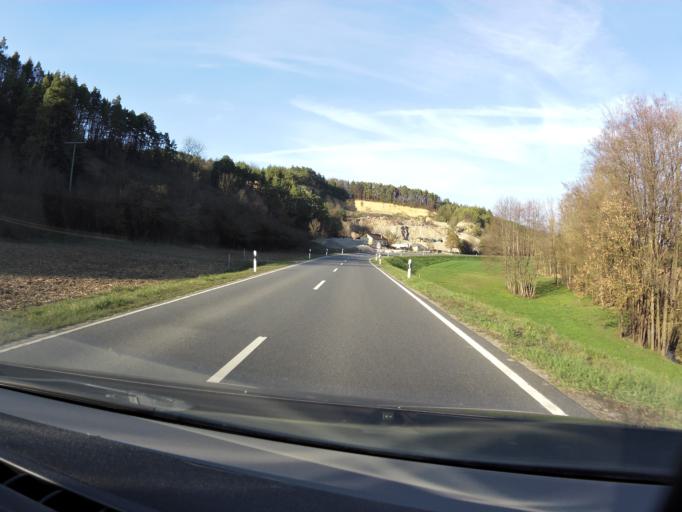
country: DE
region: Baden-Wuerttemberg
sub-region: Regierungsbezirk Stuttgart
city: Bad Mergentheim
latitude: 49.5325
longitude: 9.7699
